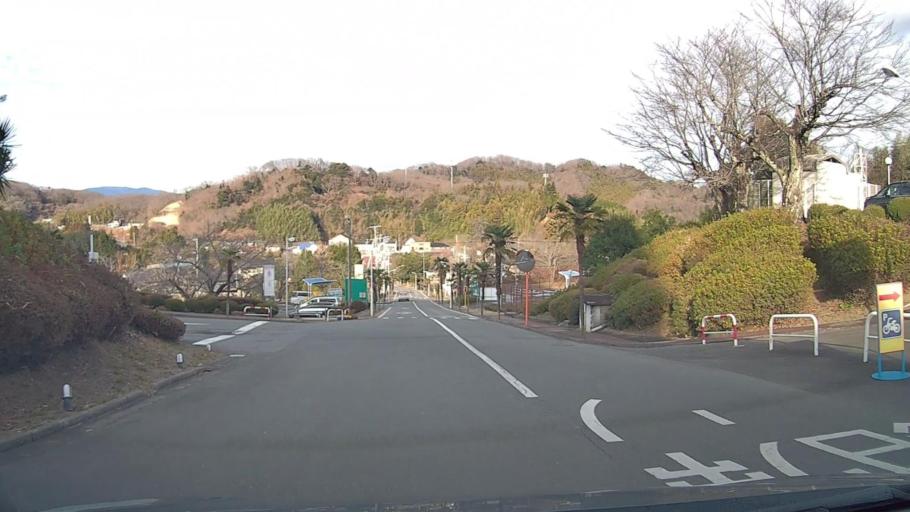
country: JP
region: Fukushima
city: Iwaki
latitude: 36.9944
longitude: 140.8178
